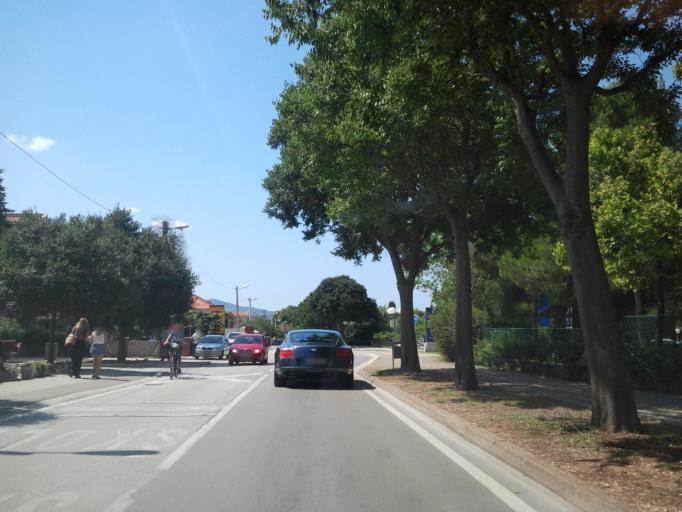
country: HR
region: Zadarska
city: Zadar
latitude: 44.1344
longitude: 15.2155
